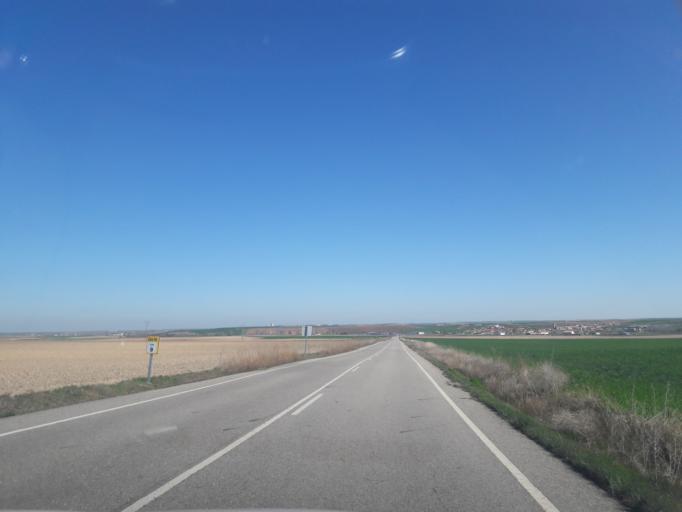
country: ES
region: Castille and Leon
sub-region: Provincia de Salamanca
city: Mancera de Abajo
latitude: 40.8237
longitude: -5.2091
